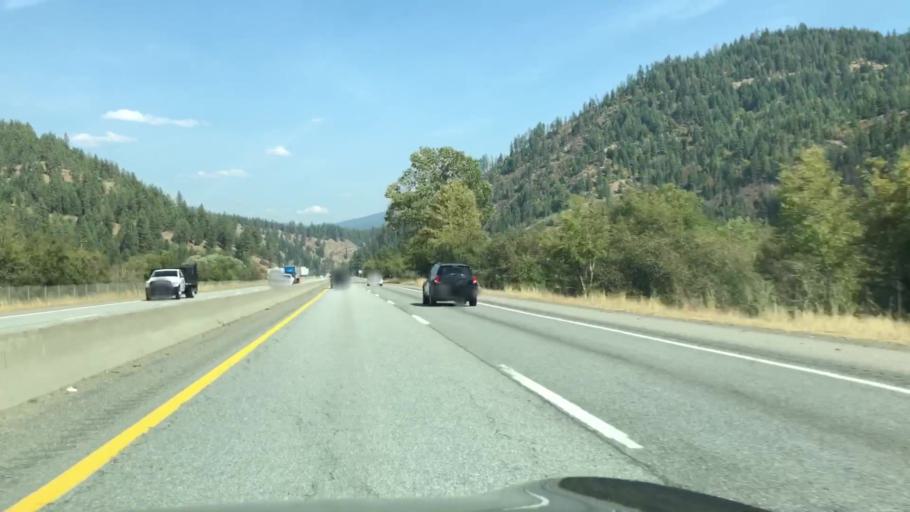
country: US
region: Idaho
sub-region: Kootenai County
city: Coeur d'Alene
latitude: 47.6270
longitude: -116.6307
